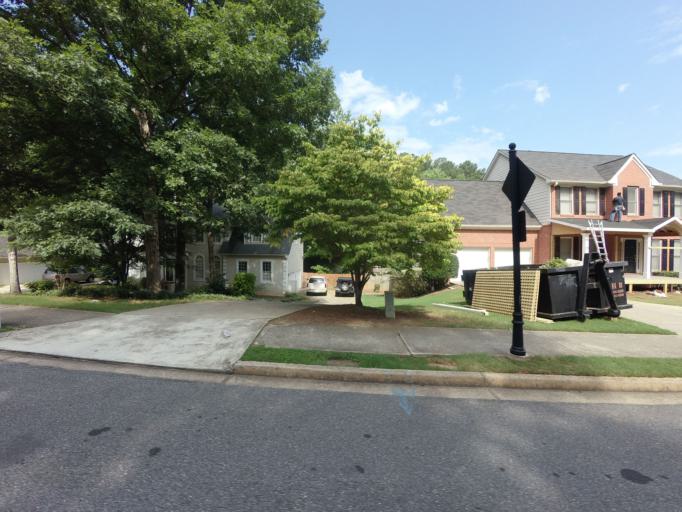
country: US
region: Georgia
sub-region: Fulton County
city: Johns Creek
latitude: 34.0408
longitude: -84.2337
